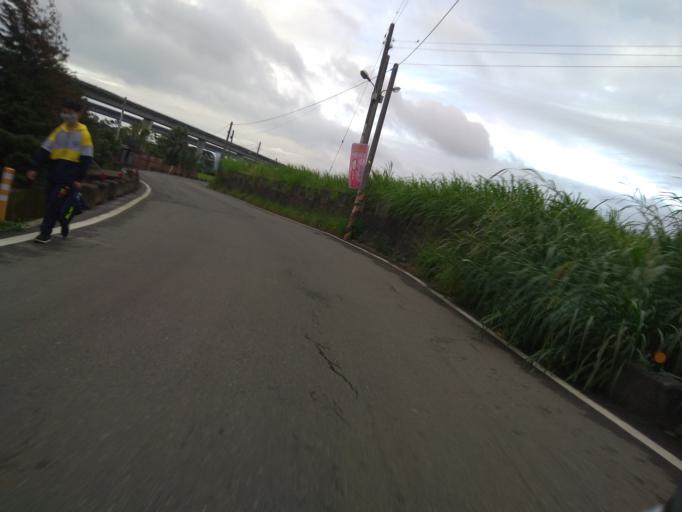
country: TW
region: Taiwan
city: Daxi
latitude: 24.9392
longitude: 121.1947
